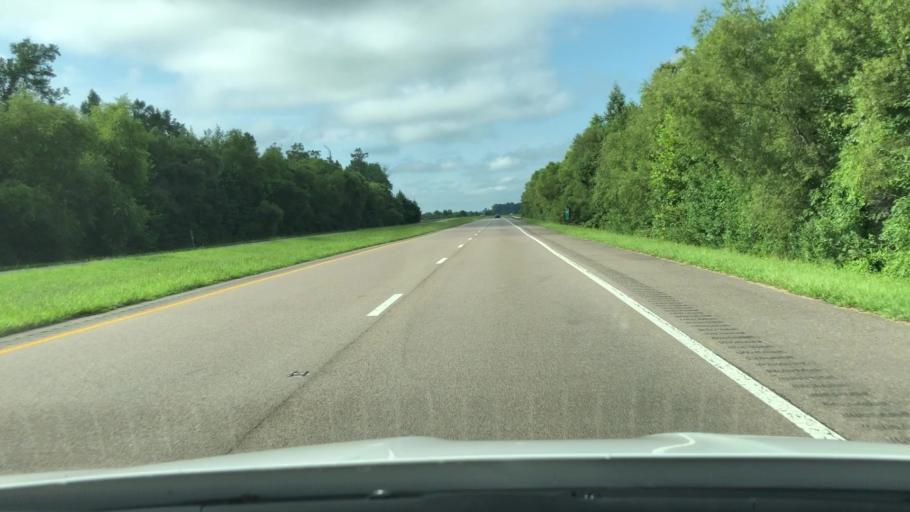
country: US
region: Virginia
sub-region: City of Portsmouth
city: Portsmouth Heights
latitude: 36.6277
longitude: -76.3647
